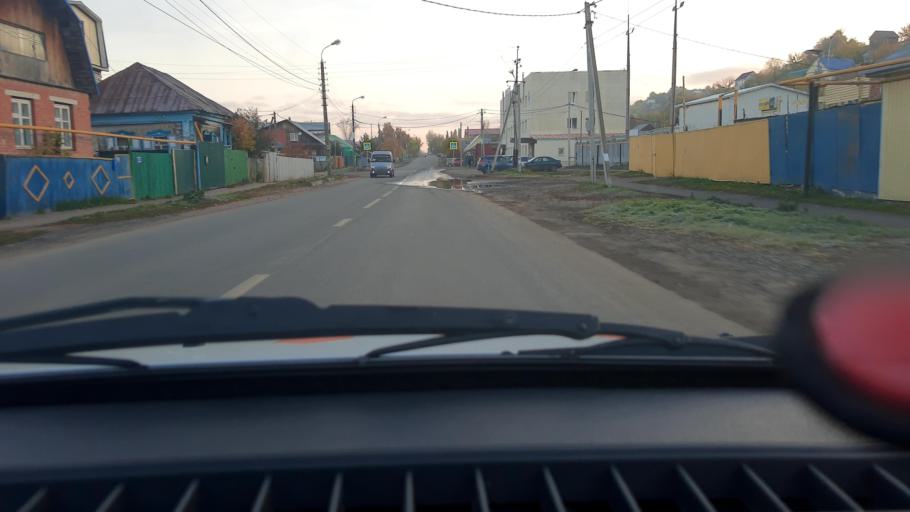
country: RU
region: Bashkortostan
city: Ufa
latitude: 54.7282
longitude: 55.9123
